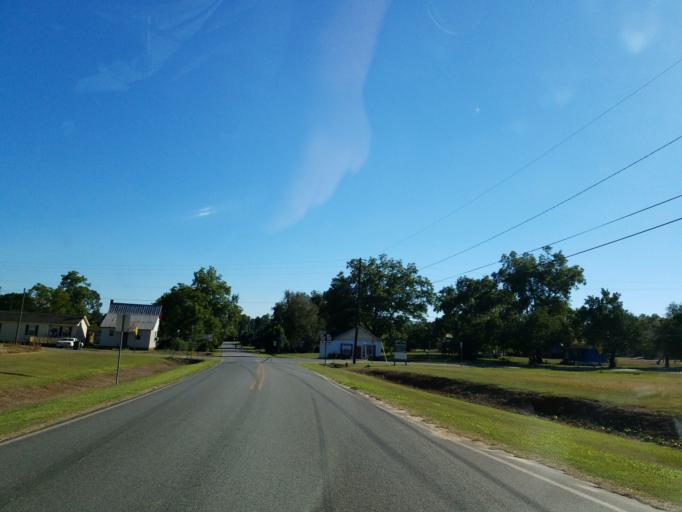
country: US
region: Georgia
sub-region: Dooly County
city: Vienna
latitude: 32.2025
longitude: -83.9039
